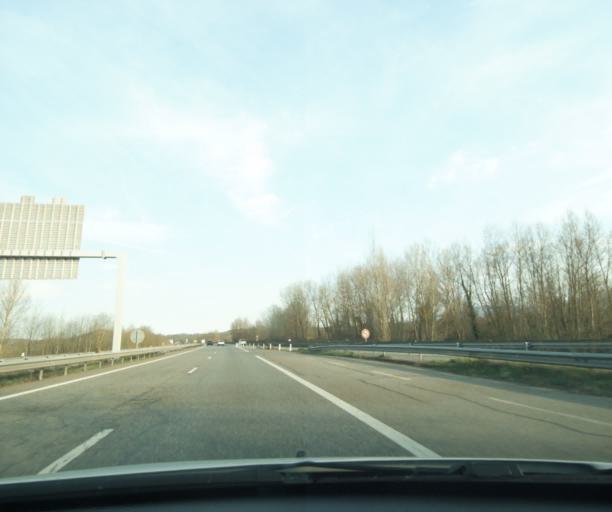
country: FR
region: Midi-Pyrenees
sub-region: Departement de la Haute-Garonne
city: Salies-du-Salat
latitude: 43.1180
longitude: 0.9008
